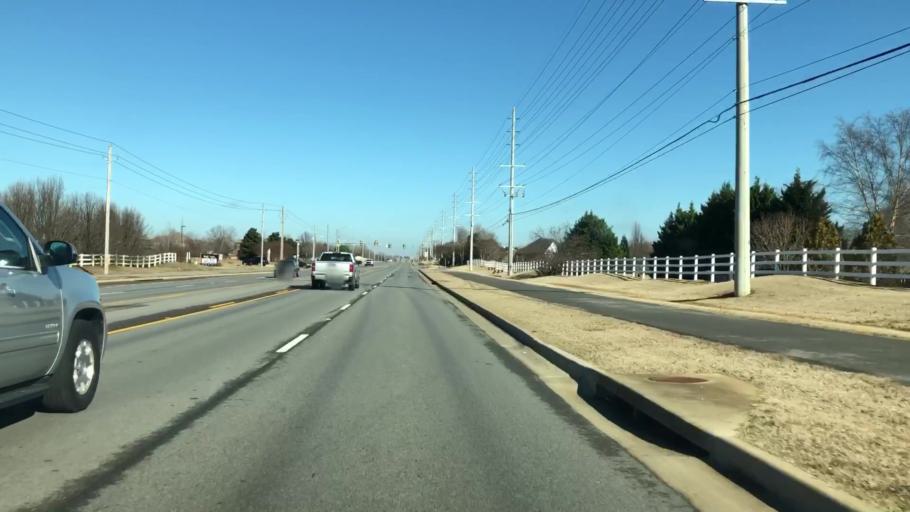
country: US
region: Alabama
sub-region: Madison County
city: Madison
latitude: 34.7062
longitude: -86.7865
